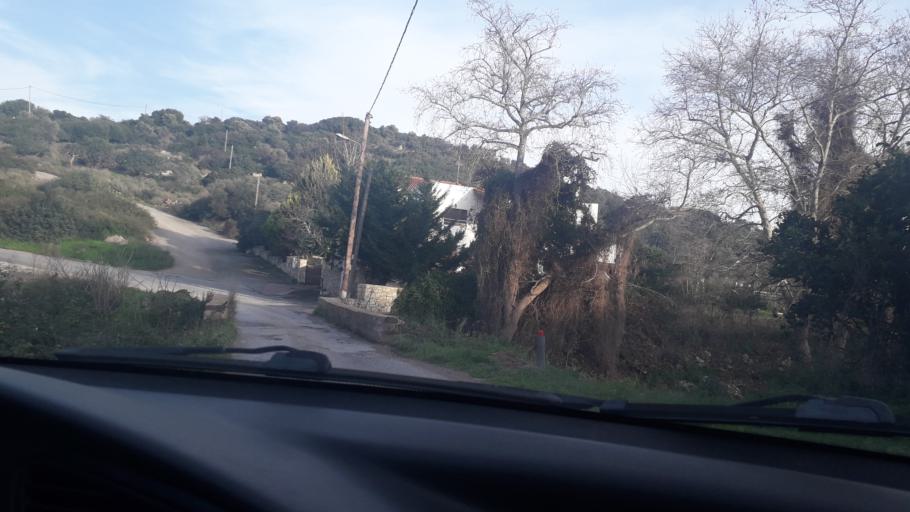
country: GR
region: Crete
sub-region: Nomos Rethymnis
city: Panormos
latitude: 35.3809
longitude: 24.6227
